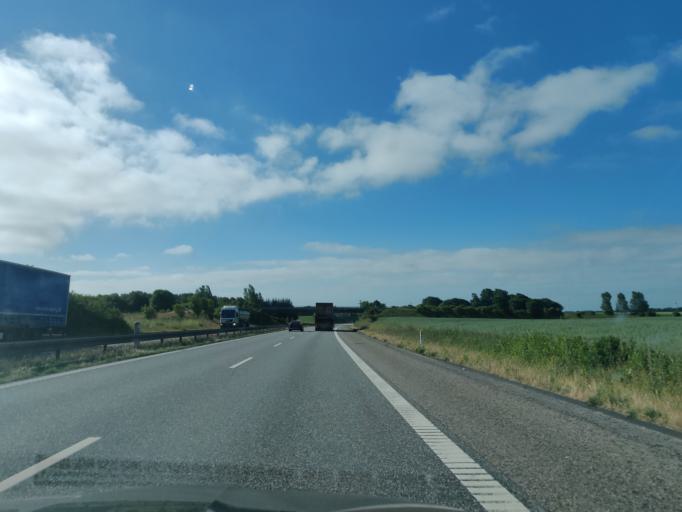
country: DK
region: North Denmark
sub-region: Mariagerfjord Kommune
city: Hobro
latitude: 56.7145
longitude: 9.7257
